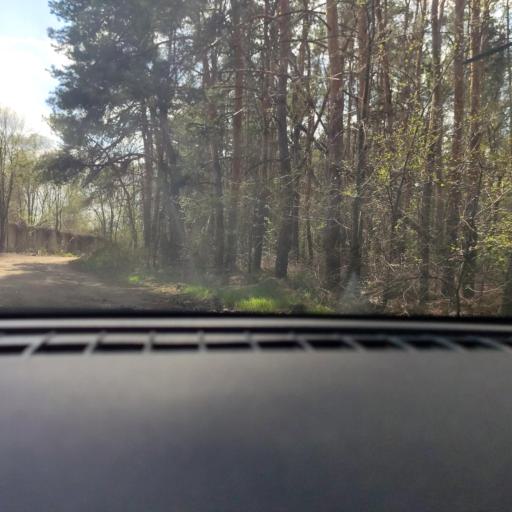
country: RU
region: Voronezj
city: Maslovka
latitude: 51.5970
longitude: 39.2194
